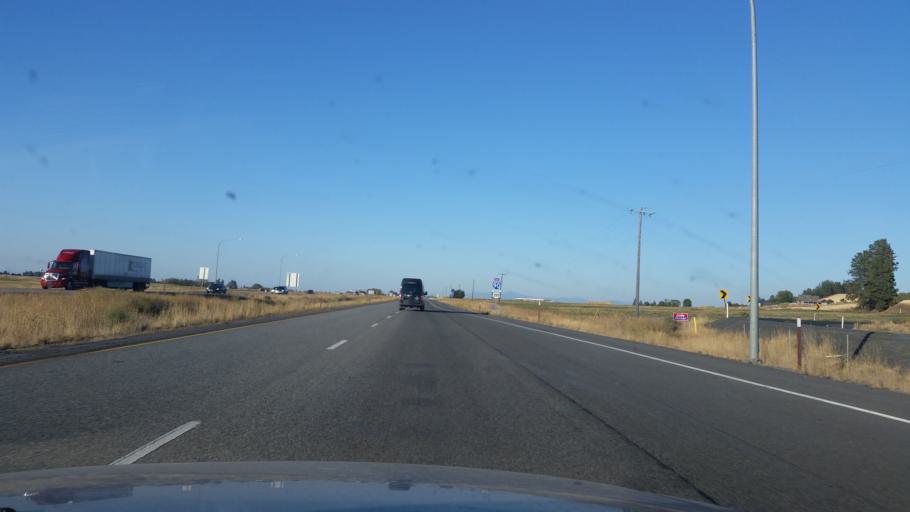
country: US
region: Washington
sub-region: Spokane County
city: Airway Heights
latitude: 47.5673
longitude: -117.5884
